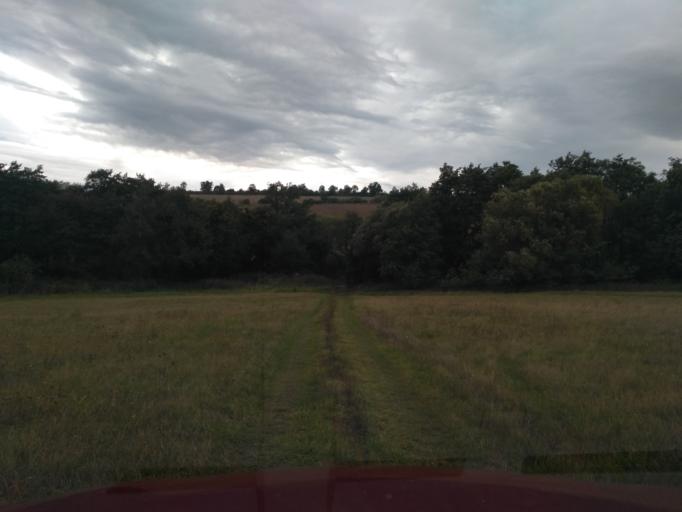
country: SK
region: Presovsky
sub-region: Okres Presov
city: Presov
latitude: 48.8976
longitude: 21.3333
